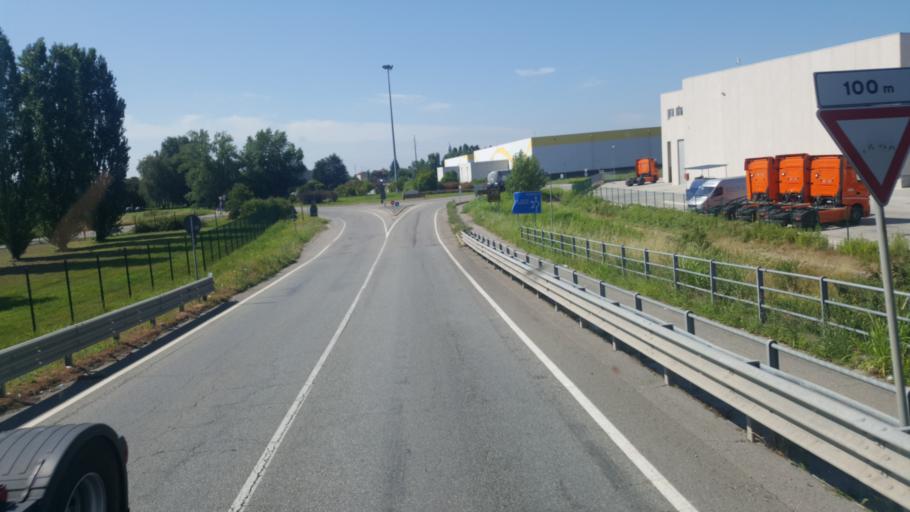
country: IT
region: Piedmont
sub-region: Provincia di Novara
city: Vicolungo
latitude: 45.4643
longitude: 8.4644
